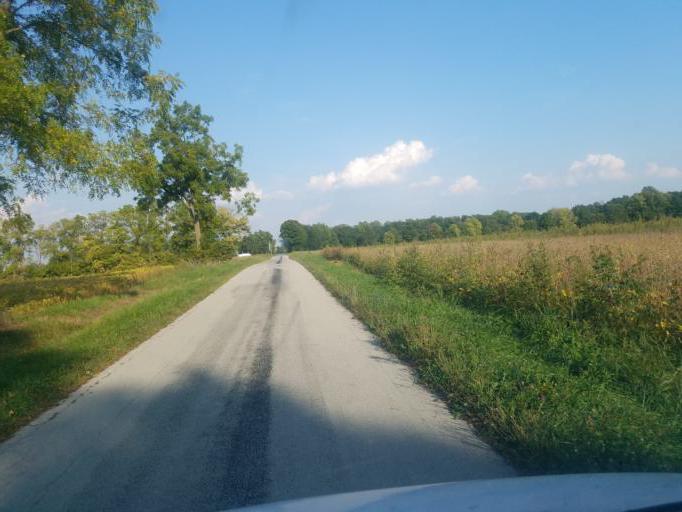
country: US
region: Ohio
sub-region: Wyandot County
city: Upper Sandusky
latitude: 40.9059
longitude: -83.2367
